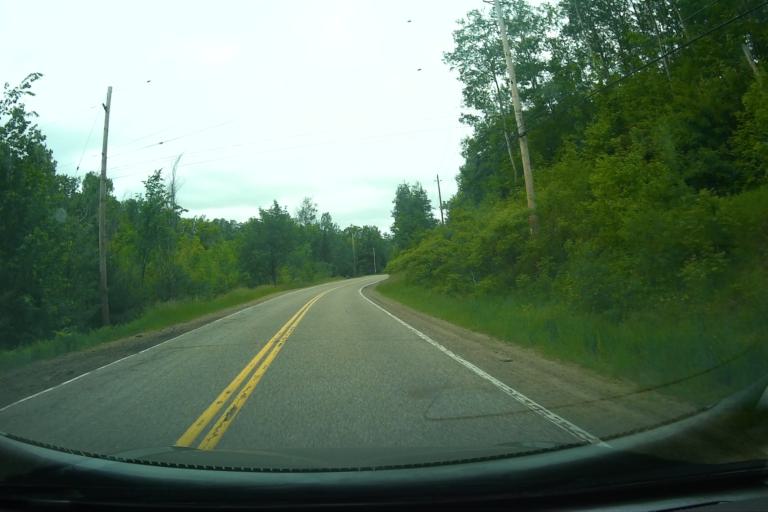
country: CA
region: Ontario
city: Pembroke
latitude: 45.4689
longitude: -77.2196
